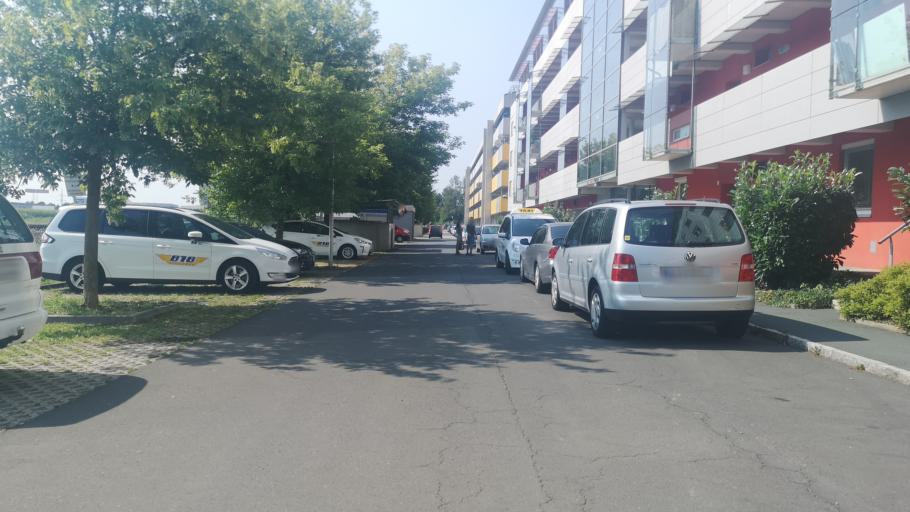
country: AT
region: Styria
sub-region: Politischer Bezirk Graz-Umgebung
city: Seiersberg
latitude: 47.0160
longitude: 15.4041
